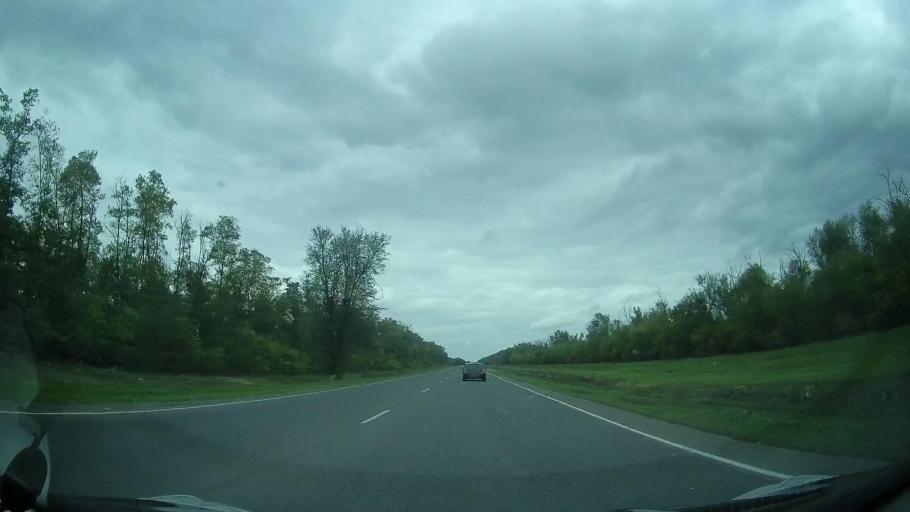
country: RU
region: Rostov
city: Yegorlykskaya
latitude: 46.5954
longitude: 40.6237
